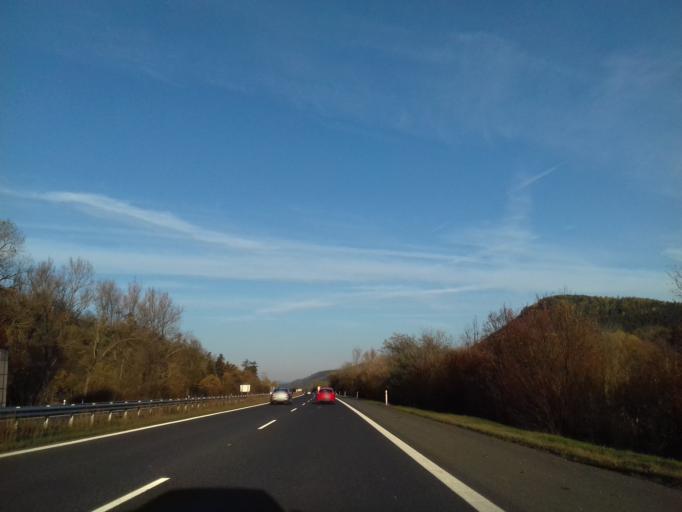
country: CZ
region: Central Bohemia
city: Zdice
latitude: 49.9150
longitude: 13.9942
